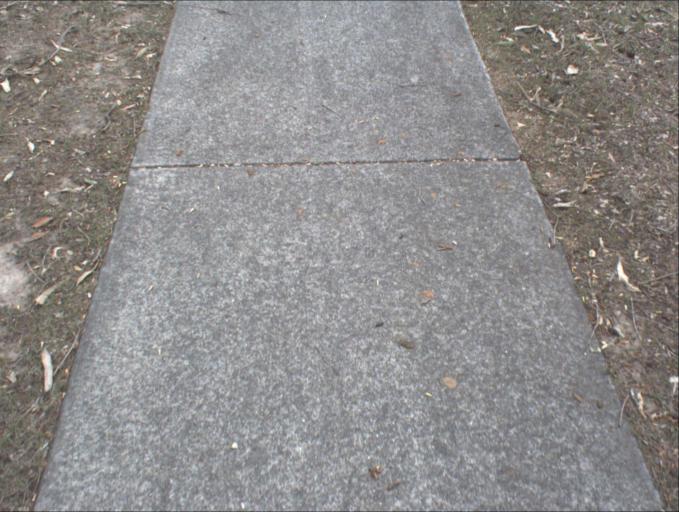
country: AU
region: Queensland
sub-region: Logan
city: Logan Reserve
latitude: -27.6841
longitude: 153.0807
